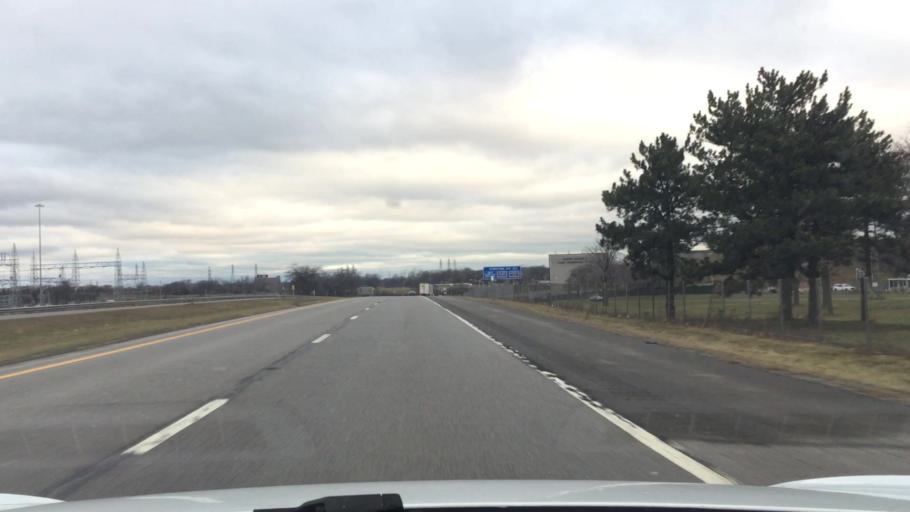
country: US
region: New York
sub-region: Niagara County
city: Lewiston
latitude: 43.1370
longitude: -79.0211
